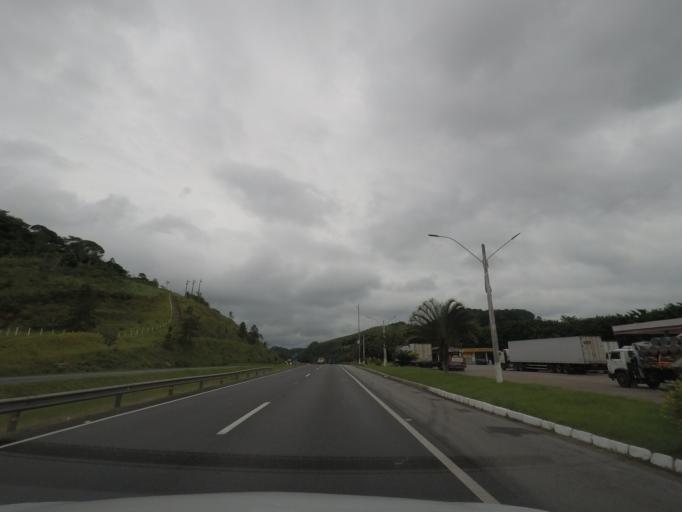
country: BR
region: Sao Paulo
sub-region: Juquia
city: Juquia
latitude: -24.3619
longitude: -47.6900
